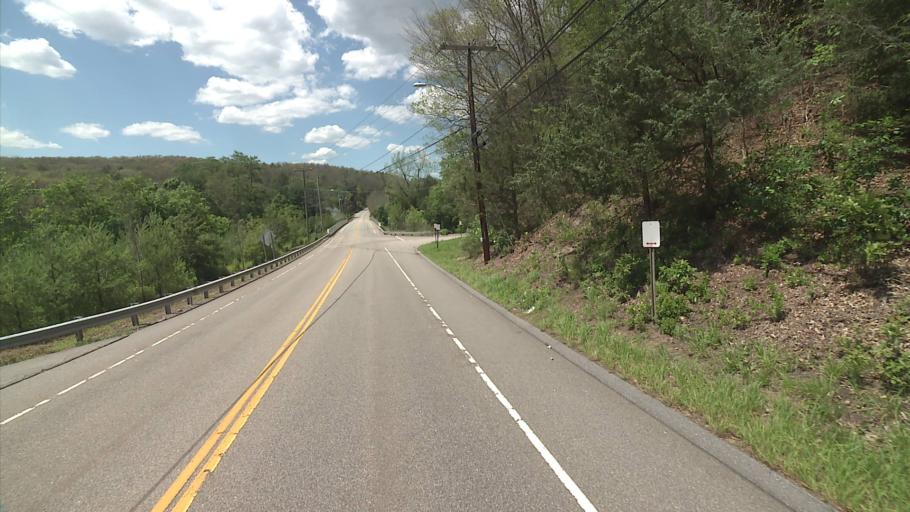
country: US
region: Connecticut
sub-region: Middlesex County
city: Moodus
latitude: 41.5114
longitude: -72.4810
